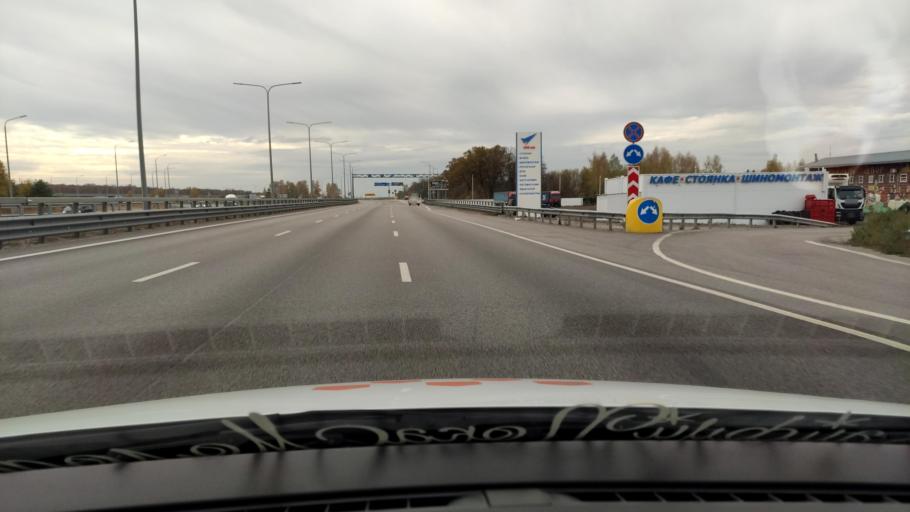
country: RU
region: Voronezj
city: Podgornoye
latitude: 51.8453
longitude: 39.2143
